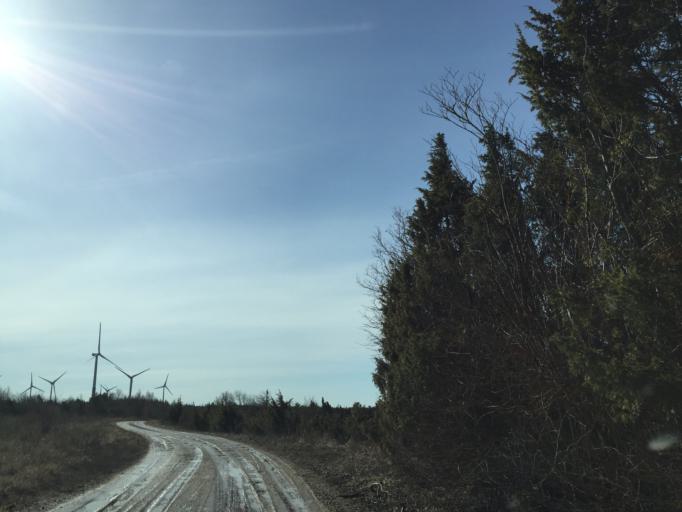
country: EE
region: Laeaene
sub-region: Haapsalu linn
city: Haapsalu
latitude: 58.6476
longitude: 23.5124
